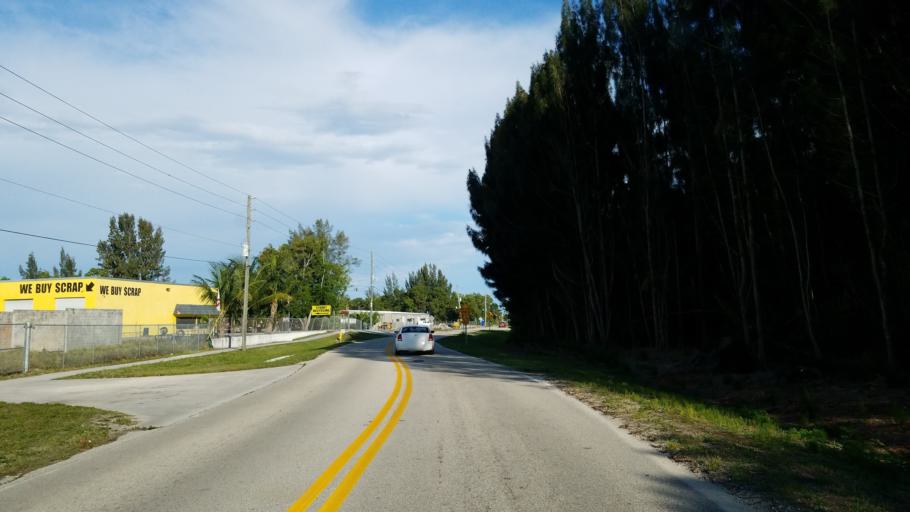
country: US
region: Florida
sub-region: Martin County
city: Port Salerno
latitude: 27.1561
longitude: -80.2130
